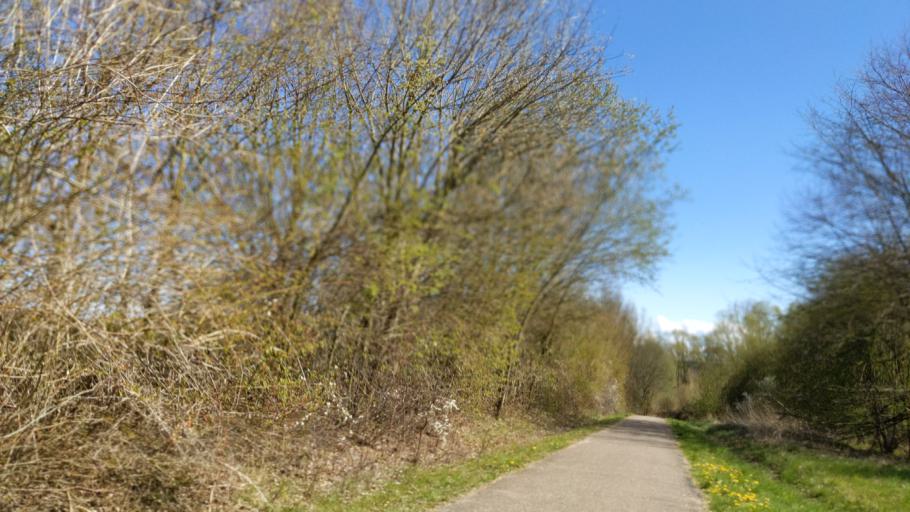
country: DE
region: Mecklenburg-Vorpommern
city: Dassow
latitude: 53.9129
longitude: 10.9671
